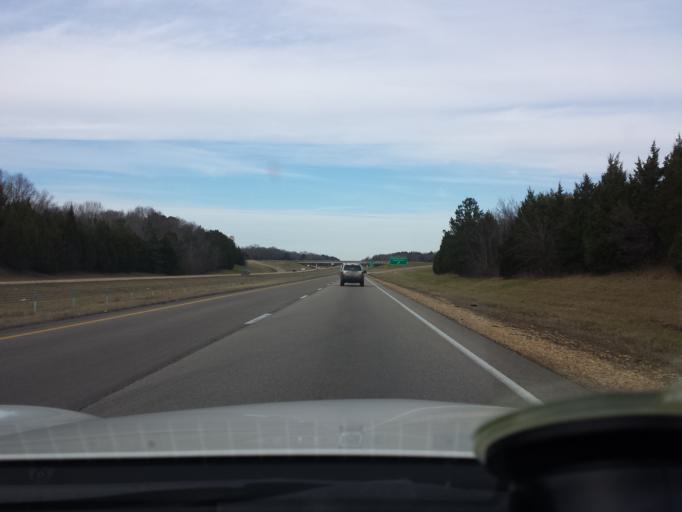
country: US
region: Mississippi
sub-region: Lee County
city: Verona
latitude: 34.1862
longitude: -88.7061
